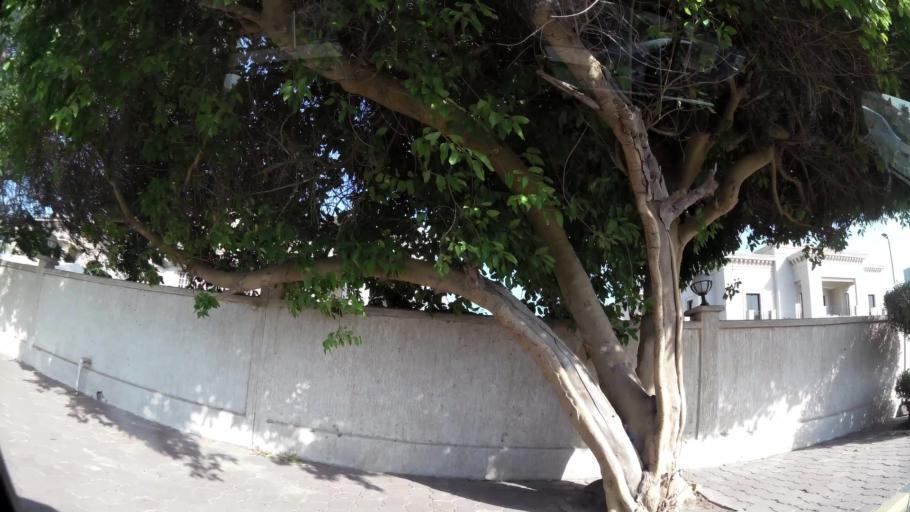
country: KW
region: Muhafazat Hawalli
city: Ar Rumaythiyah
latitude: 29.3114
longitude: 48.0868
